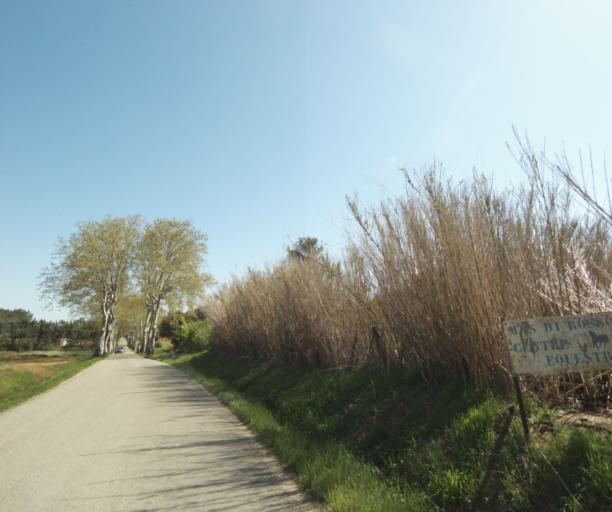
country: FR
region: Languedoc-Roussillon
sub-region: Departement de l'Herault
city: Saint-Drezery
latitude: 43.7211
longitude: 3.9876
